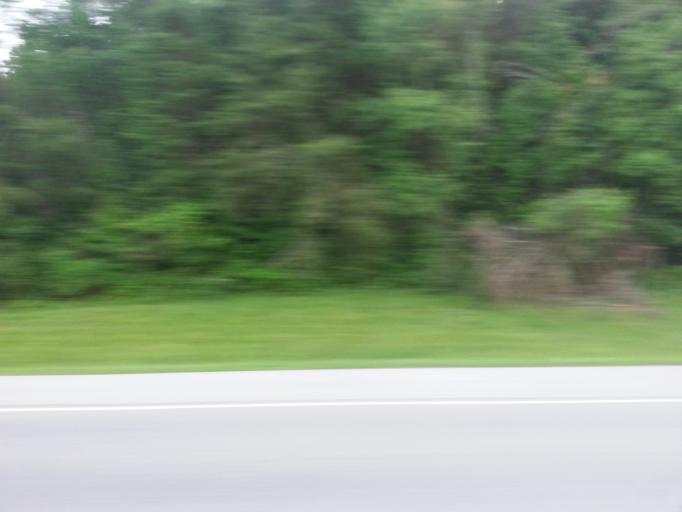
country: US
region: Tennessee
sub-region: Monroe County
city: Madisonville
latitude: 35.3710
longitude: -84.3030
